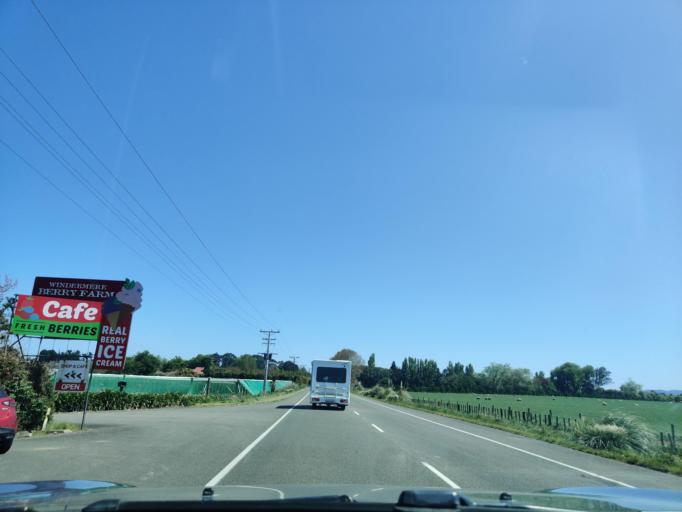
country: NZ
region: Manawatu-Wanganui
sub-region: Wanganui District
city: Wanganui
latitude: -39.8730
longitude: 174.9931
